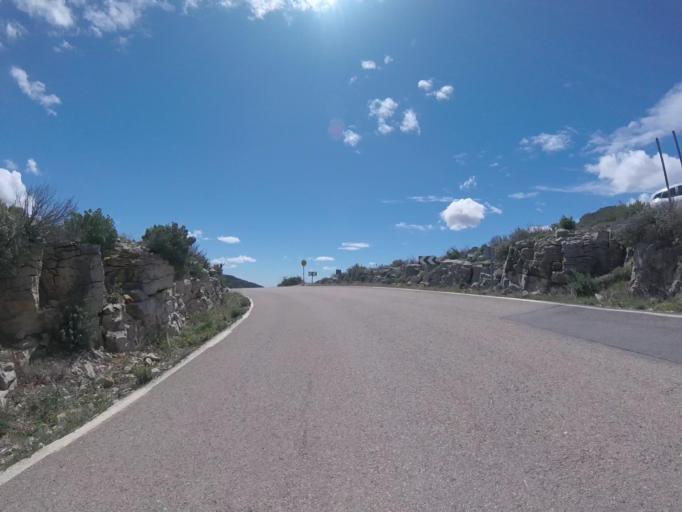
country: ES
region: Valencia
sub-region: Provincia de Castello
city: Sierra-Engarceran
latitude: 40.2759
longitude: -0.0328
